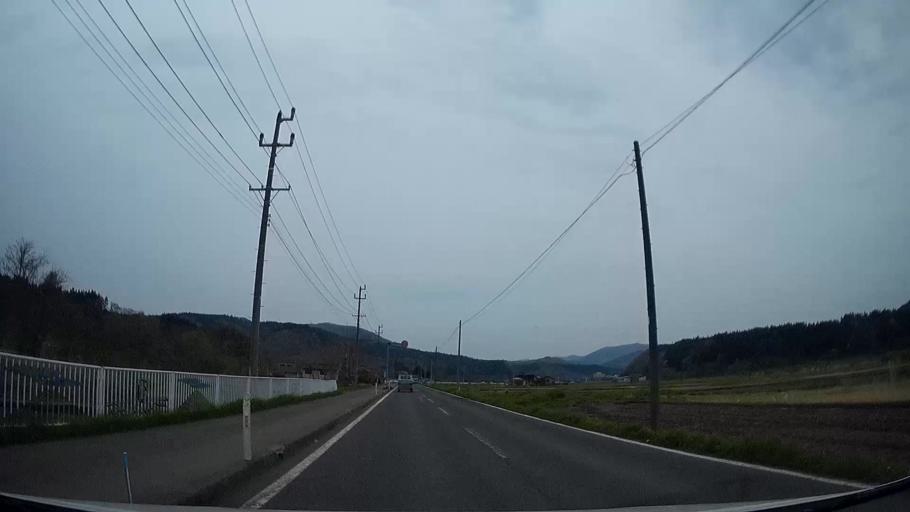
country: JP
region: Akita
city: Hanawa
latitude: 40.2836
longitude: 140.8030
